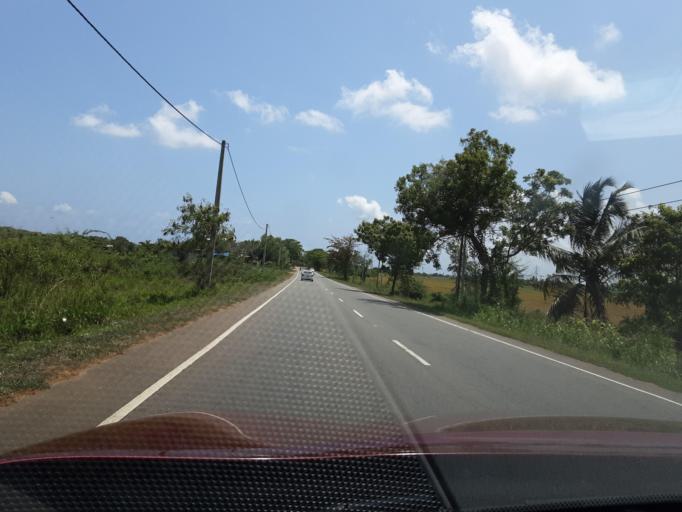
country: LK
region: Southern
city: Tangalla
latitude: 6.2247
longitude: 81.2201
